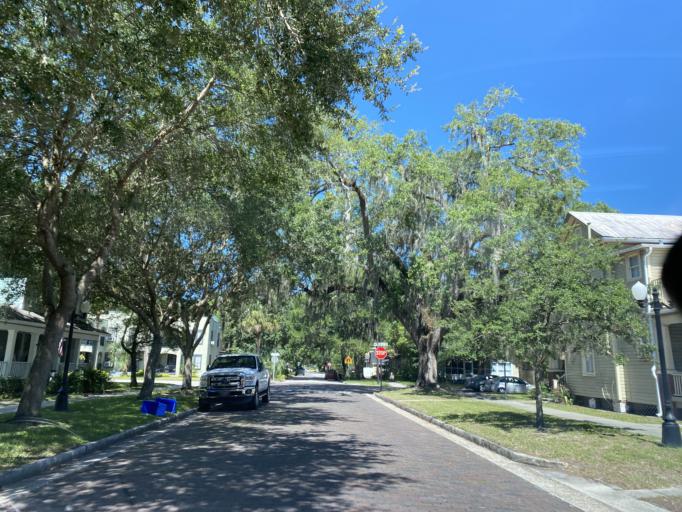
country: US
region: Florida
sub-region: Seminole County
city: Sanford
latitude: 28.8036
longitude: -81.2675
